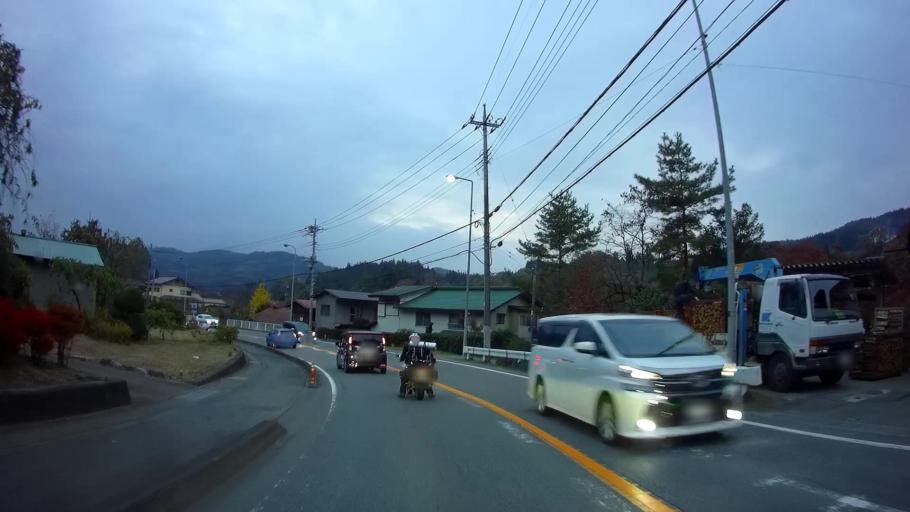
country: JP
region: Gunma
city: Nakanojomachi
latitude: 36.5523
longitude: 138.7828
